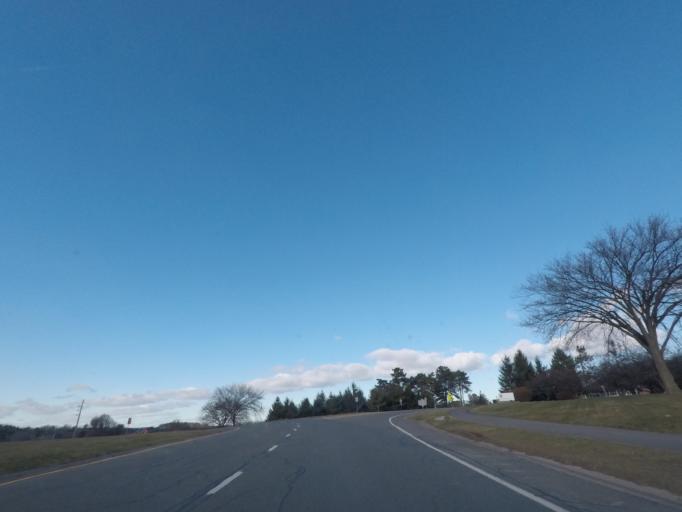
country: US
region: New York
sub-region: Schenectady County
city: Niskayuna
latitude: 42.8257
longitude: -73.8783
